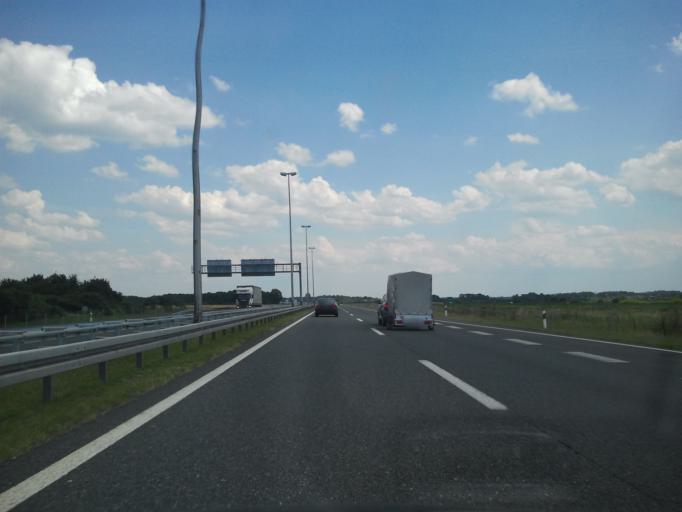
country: HR
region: Brodsko-Posavska
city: Bukovlje
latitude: 45.1772
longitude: 18.0738
